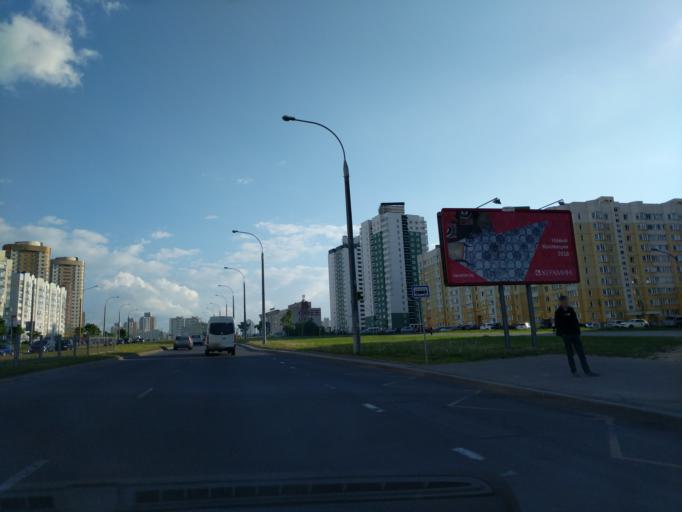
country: BY
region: Minsk
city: Zhdanovichy
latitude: 53.9238
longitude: 27.4397
